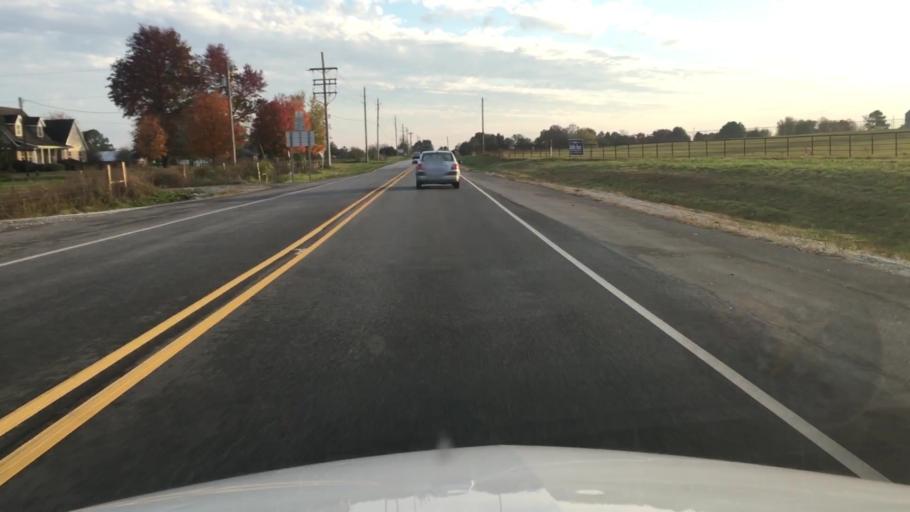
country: US
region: Arkansas
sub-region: Washington County
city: Elm Springs
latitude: 36.2243
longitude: -94.2303
